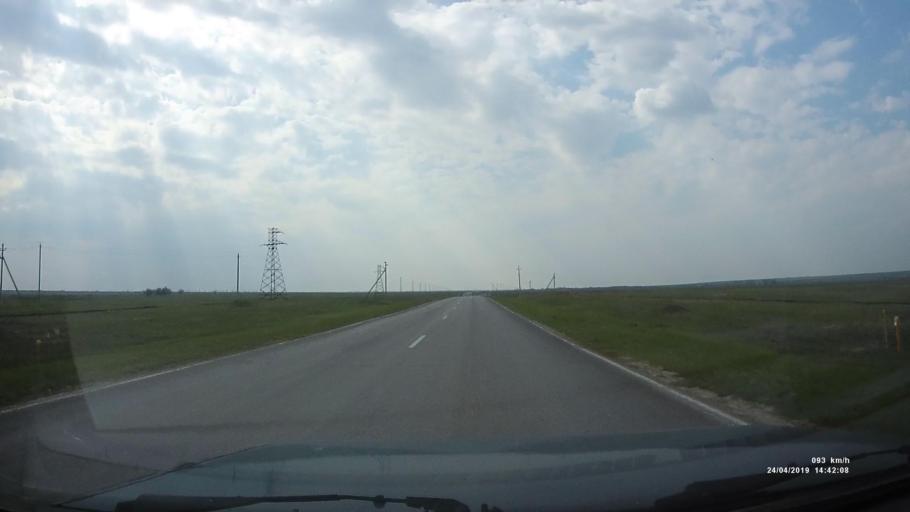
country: RU
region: Rostov
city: Remontnoye
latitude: 46.4505
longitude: 43.8680
